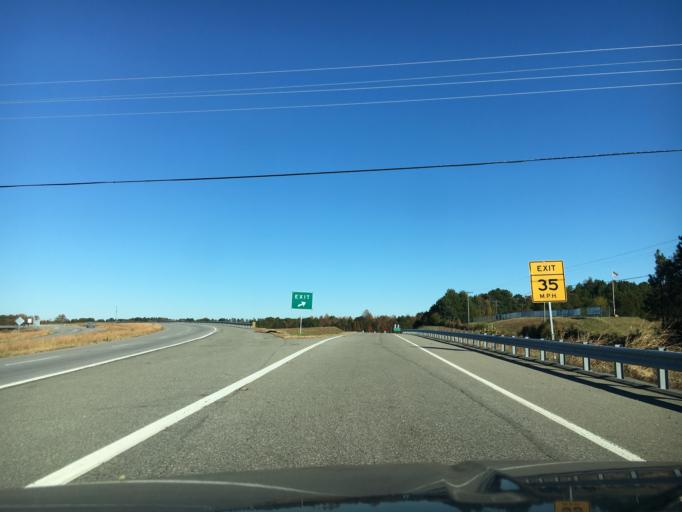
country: US
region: Virginia
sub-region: Mecklenburg County
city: Clarksville
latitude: 36.6052
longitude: -78.5687
